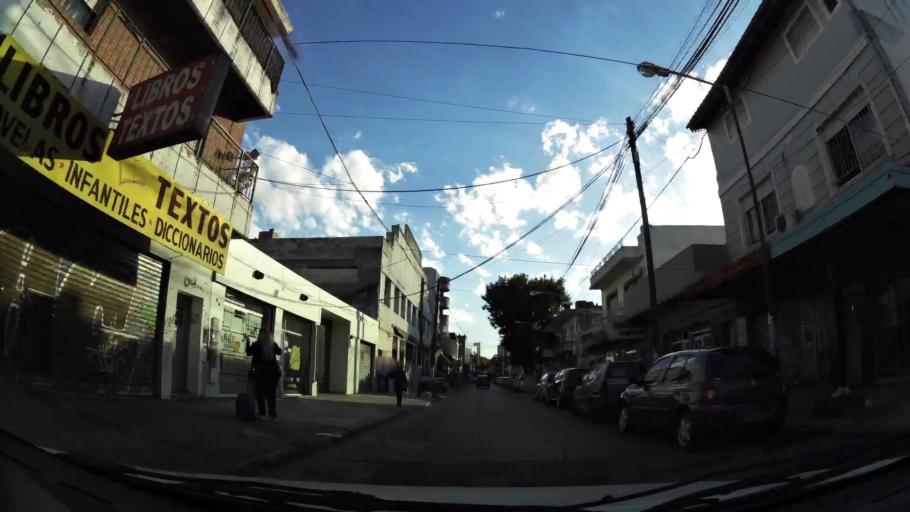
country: AR
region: Buenos Aires
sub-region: Partido de General San Martin
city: General San Martin
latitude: -34.5519
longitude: -58.5558
